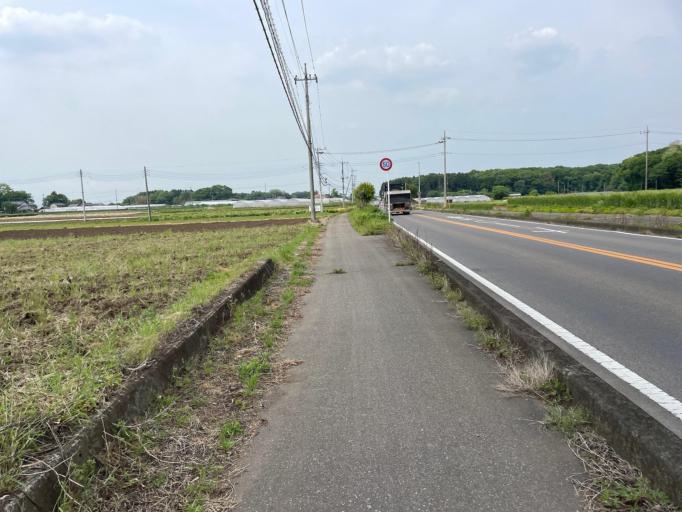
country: JP
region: Tochigi
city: Mibu
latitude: 36.3778
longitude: 139.8042
